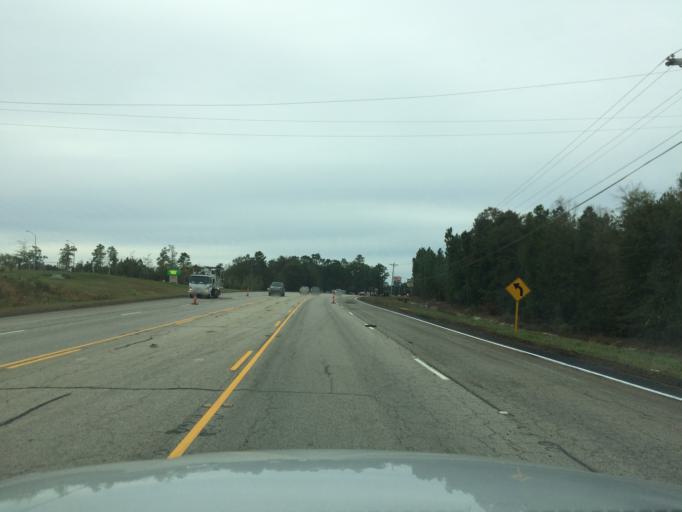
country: US
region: South Carolina
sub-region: Aiken County
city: Aiken
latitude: 33.6023
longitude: -81.6861
